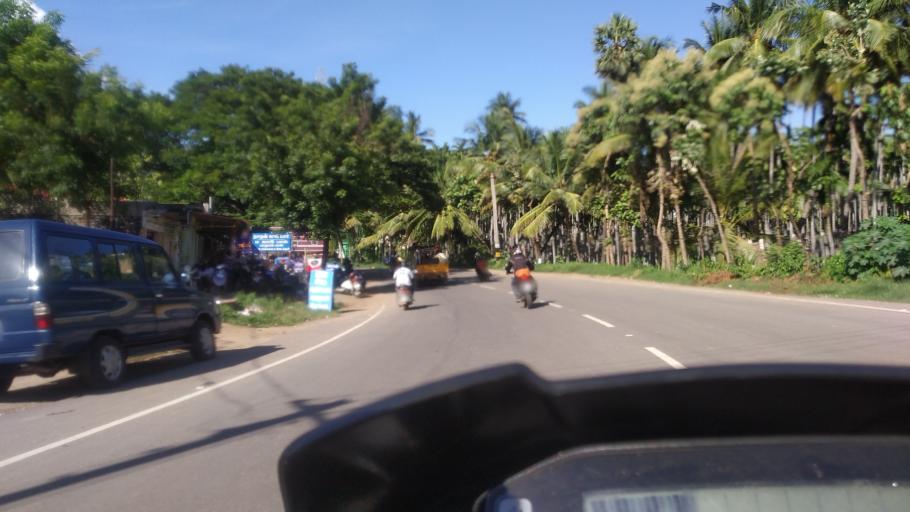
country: IN
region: Tamil Nadu
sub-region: Salem
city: Salem
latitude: 11.7080
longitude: 78.1764
